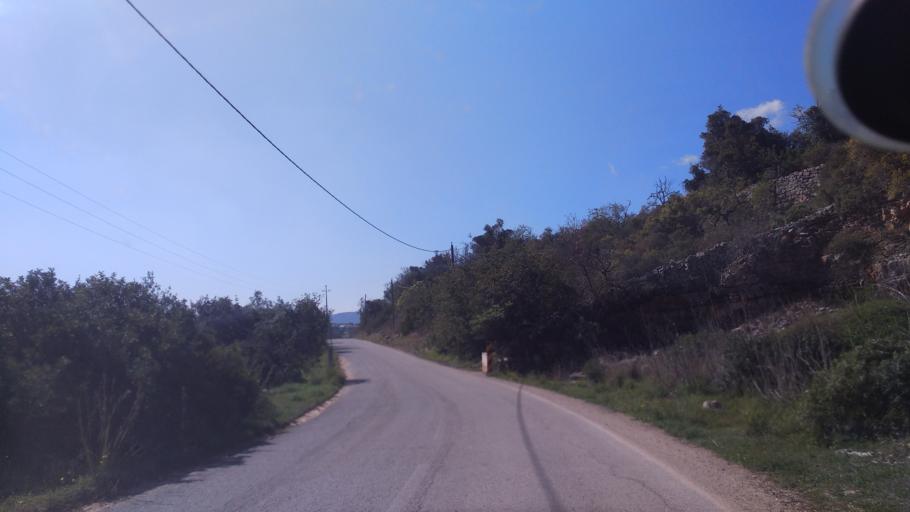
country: PT
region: Faro
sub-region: Sao Bras de Alportel
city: Sao Bras de Alportel
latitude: 37.1350
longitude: -7.9114
